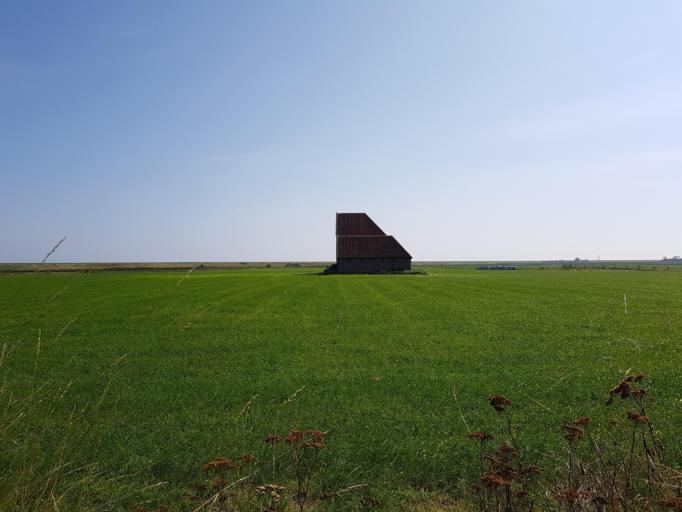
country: NL
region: North Holland
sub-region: Gemeente Texel
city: Den Burg
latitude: 53.0925
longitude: 4.8903
